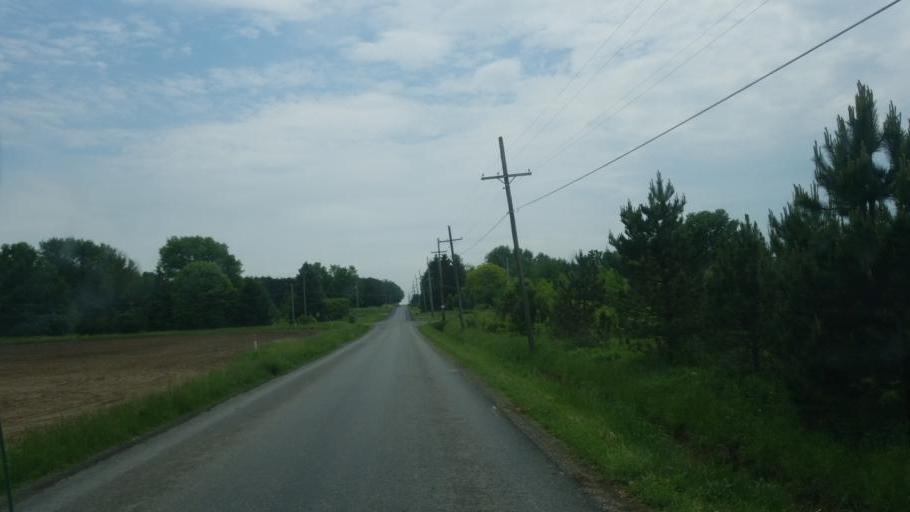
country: US
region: Ohio
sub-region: Wayne County
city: Orrville
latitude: 40.7838
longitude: -81.7552
